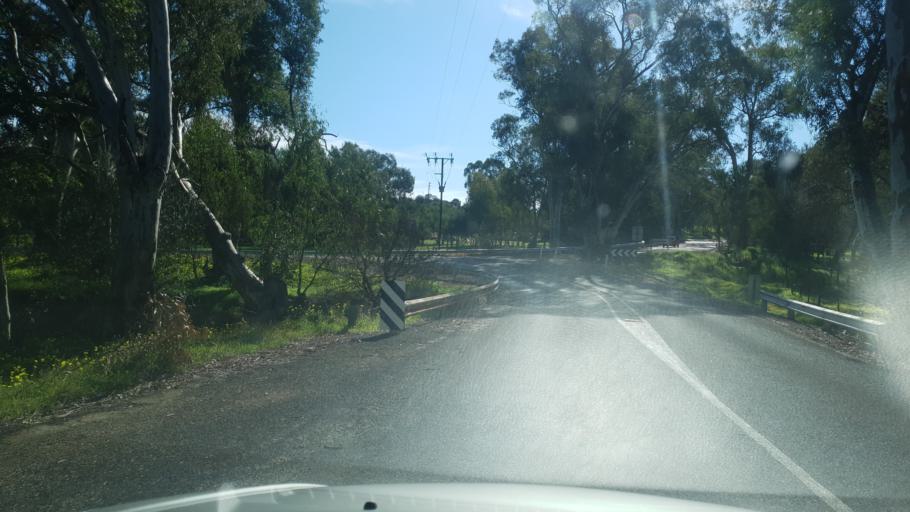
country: AU
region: South Australia
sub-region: Barossa
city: Lyndoch
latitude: -34.6270
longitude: 138.8445
